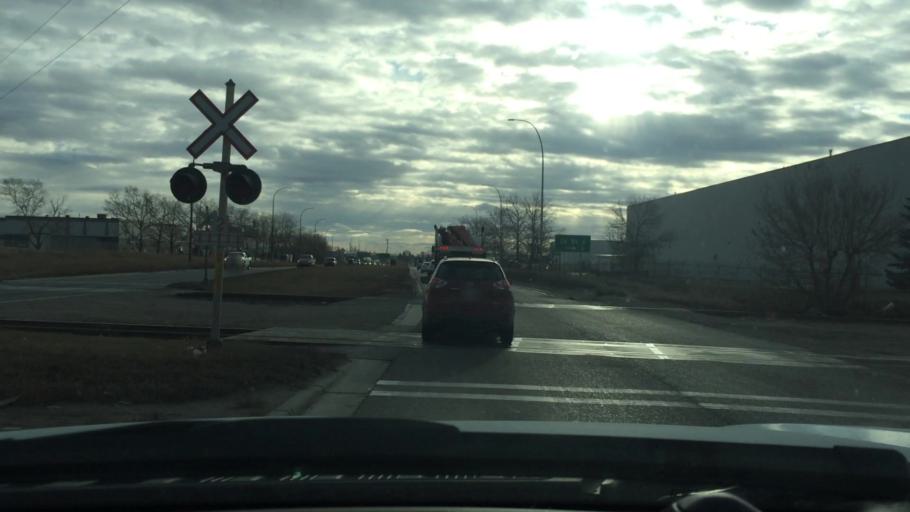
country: CA
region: Alberta
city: Calgary
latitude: 51.0067
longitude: -113.9999
